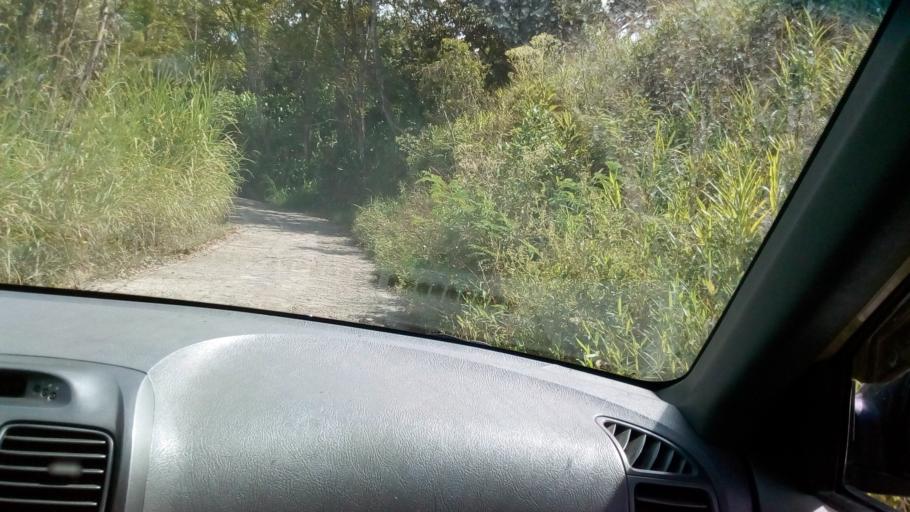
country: CO
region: Cundinamarca
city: Tenza
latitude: 5.0938
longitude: -73.4247
